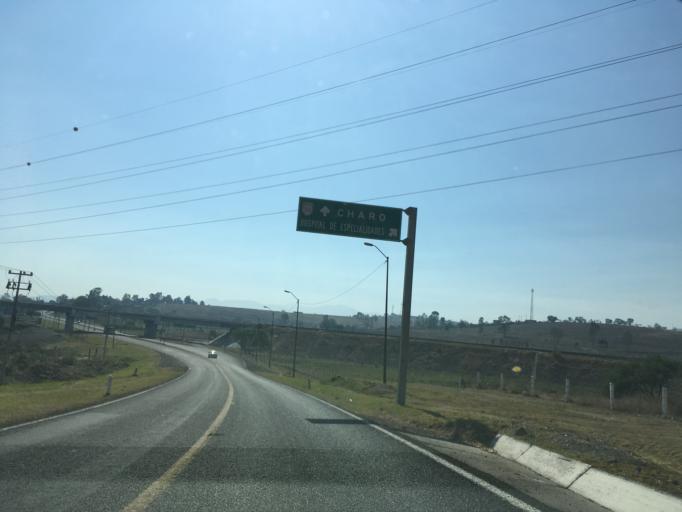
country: MX
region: Michoacan
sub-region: Morelia
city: La Aldea
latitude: 19.7361
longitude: -101.1061
